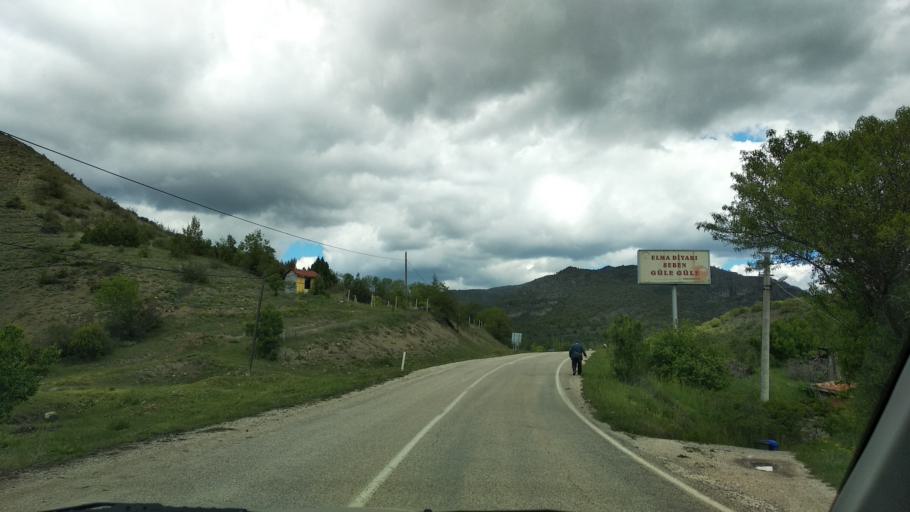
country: TR
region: Bolu
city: Seben
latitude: 40.4206
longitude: 31.5844
